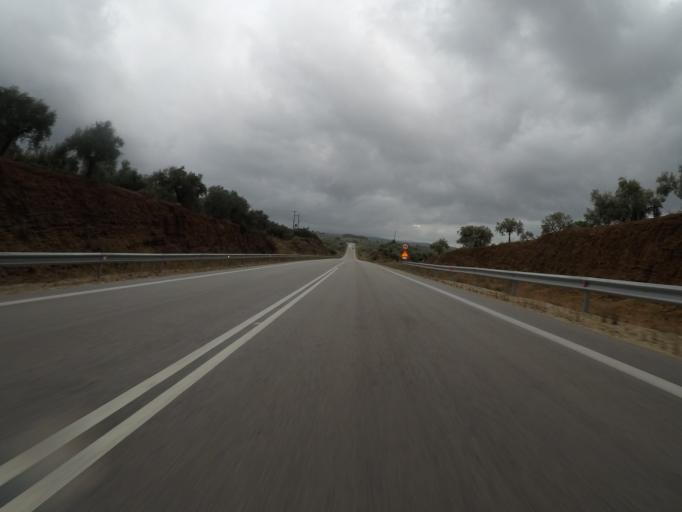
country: GR
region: Peloponnese
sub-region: Nomos Messinias
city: Gargalianoi
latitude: 37.0146
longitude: 21.6477
